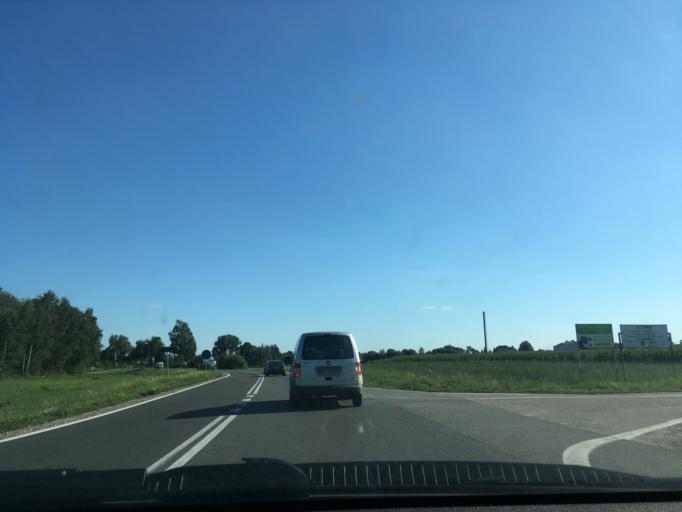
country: PL
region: Podlasie
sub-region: Powiat sokolski
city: Suchowola
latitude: 53.4527
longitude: 23.0873
